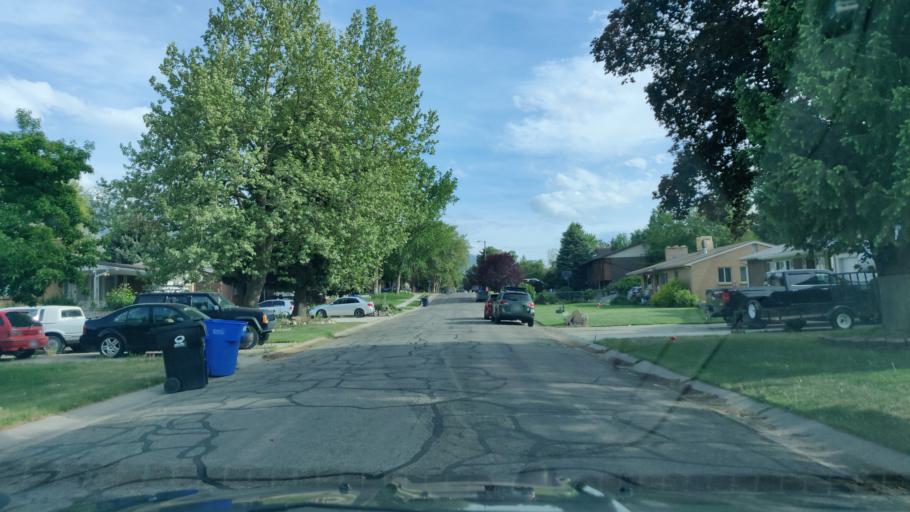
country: US
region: Utah
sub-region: Salt Lake County
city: Cottonwood Heights
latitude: 40.6219
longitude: -111.8134
